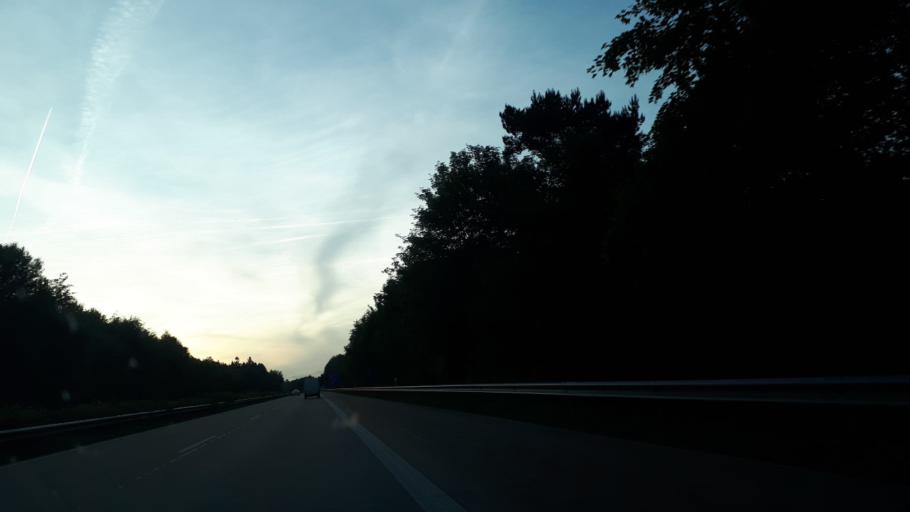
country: DE
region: Rheinland-Pfalz
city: Laubach
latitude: 50.2317
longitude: 7.0921
